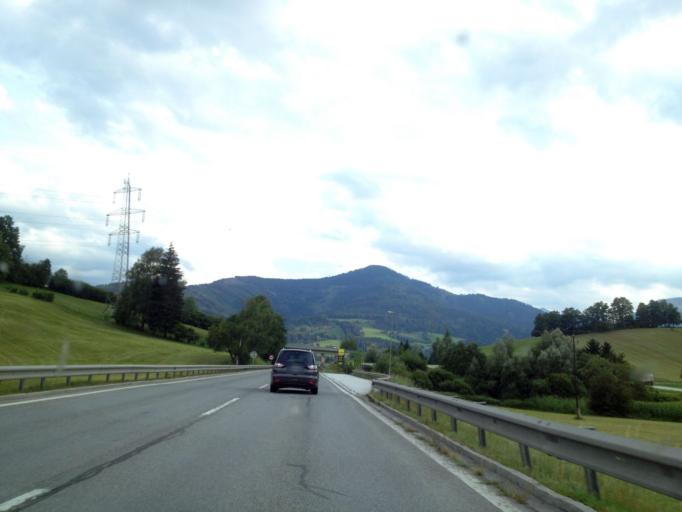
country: AT
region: Styria
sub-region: Politischer Bezirk Liezen
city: Grobming
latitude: 47.4482
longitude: 13.9127
